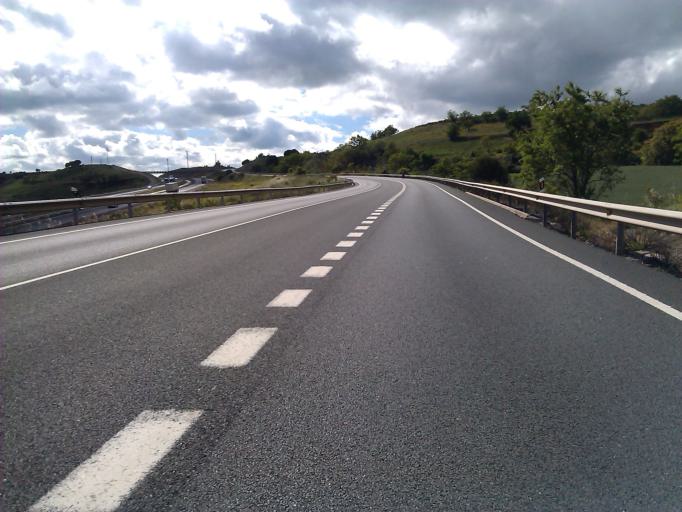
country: ES
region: La Rioja
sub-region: Provincia de La Rioja
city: Hervias
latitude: 42.4395
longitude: -2.8551
